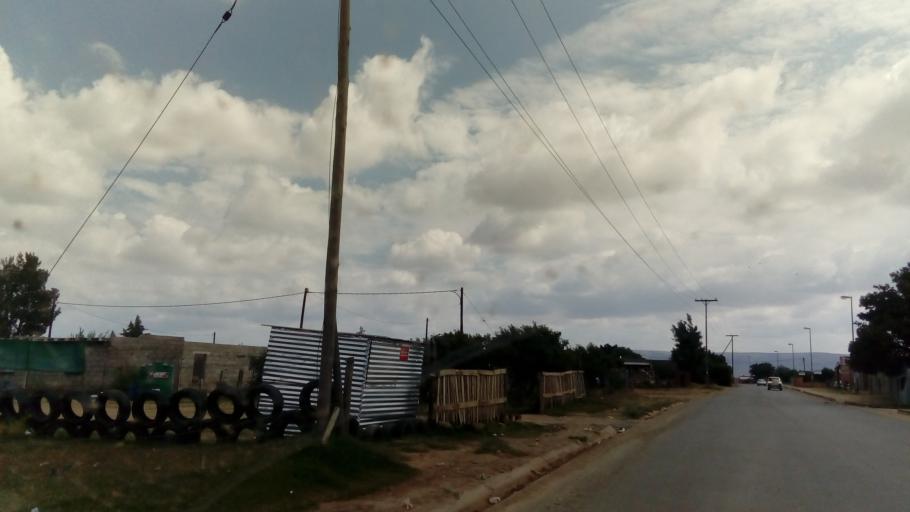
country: LS
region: Maseru
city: Maseru
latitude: -29.3818
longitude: 27.5300
